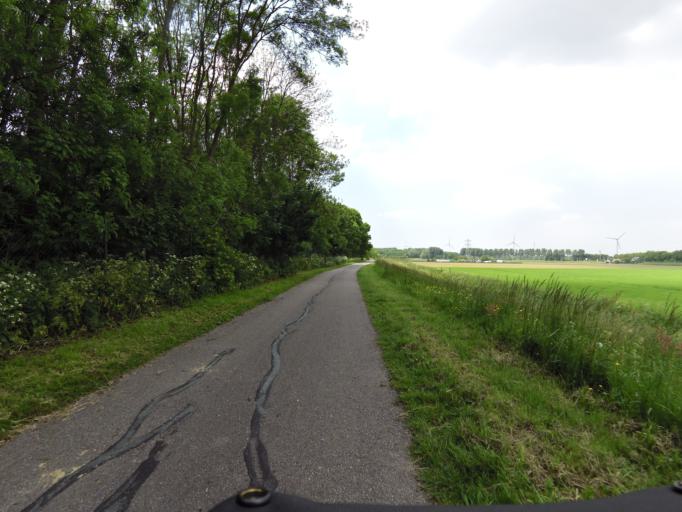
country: NL
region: South Holland
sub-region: Gemeente Maassluis
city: Maassluis
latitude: 51.8517
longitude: 4.2493
